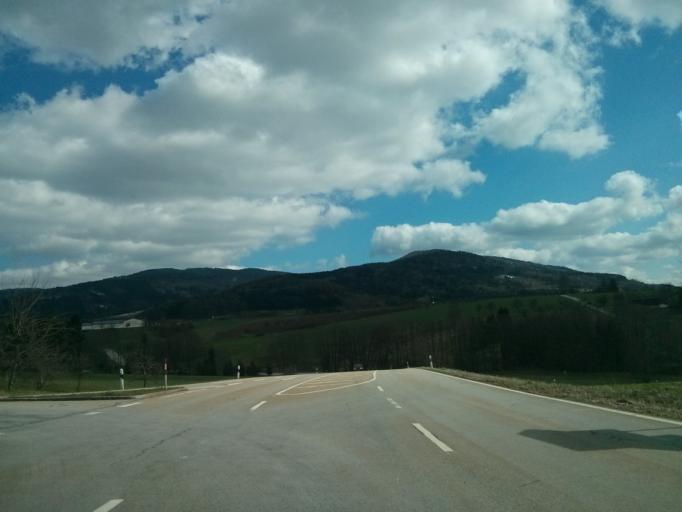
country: DE
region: Bavaria
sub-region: Lower Bavaria
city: Lalling
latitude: 48.8413
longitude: 13.1413
